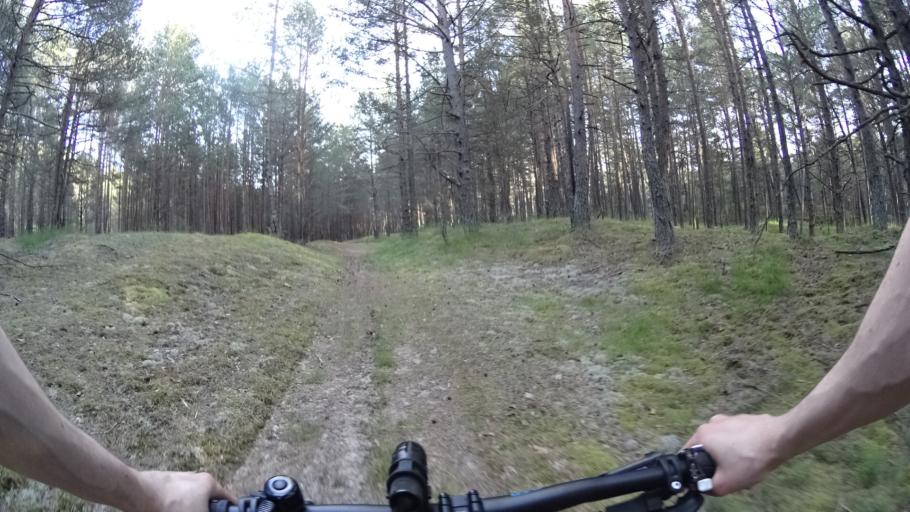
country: LV
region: Riga
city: Jaunciems
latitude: 57.1089
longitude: 24.1885
